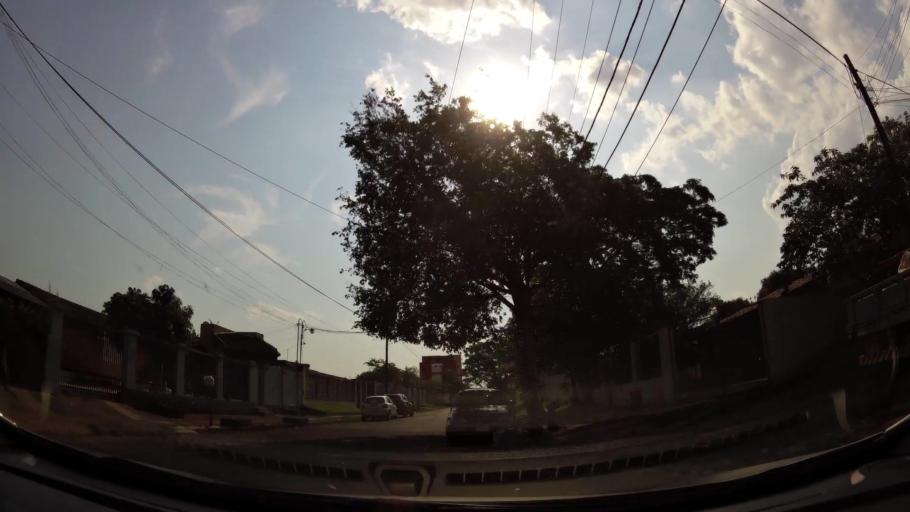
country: PY
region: Alto Parana
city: Presidente Franco
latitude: -25.5315
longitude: -54.6244
